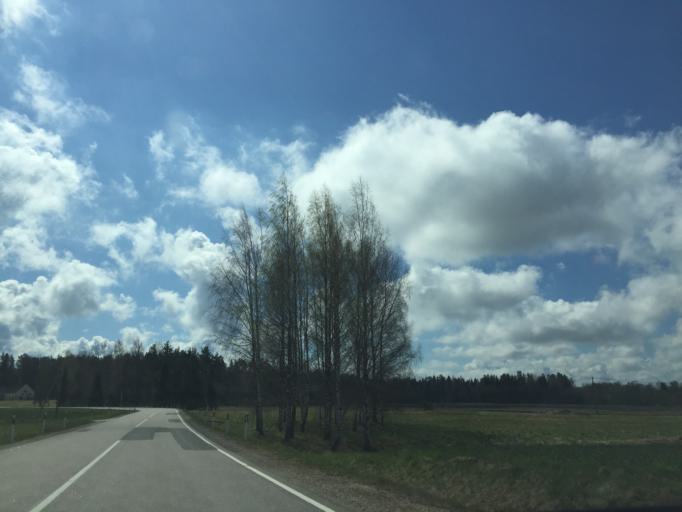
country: LV
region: Apes Novads
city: Ape
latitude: 57.5259
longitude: 26.6989
